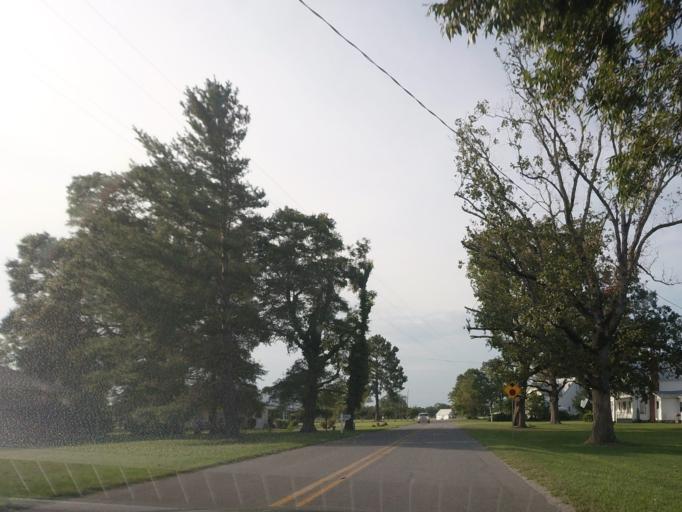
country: US
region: Georgia
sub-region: Bleckley County
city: Cochran
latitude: 32.5130
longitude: -83.3045
